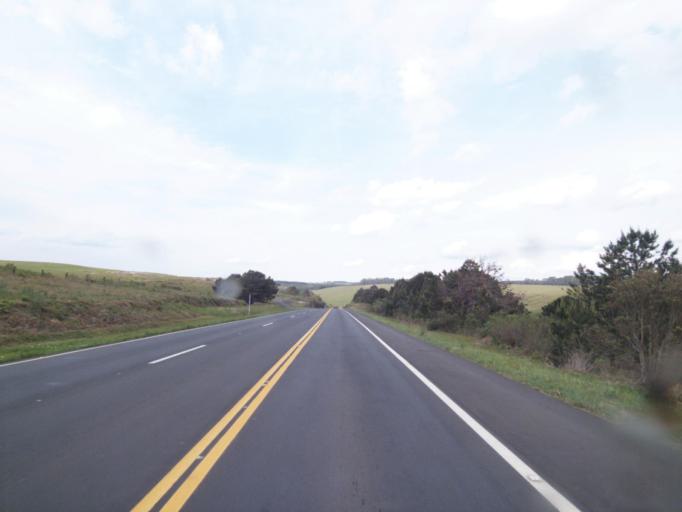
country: BR
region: Parana
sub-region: Palmeira
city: Palmeira
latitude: -25.4695
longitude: -49.7737
